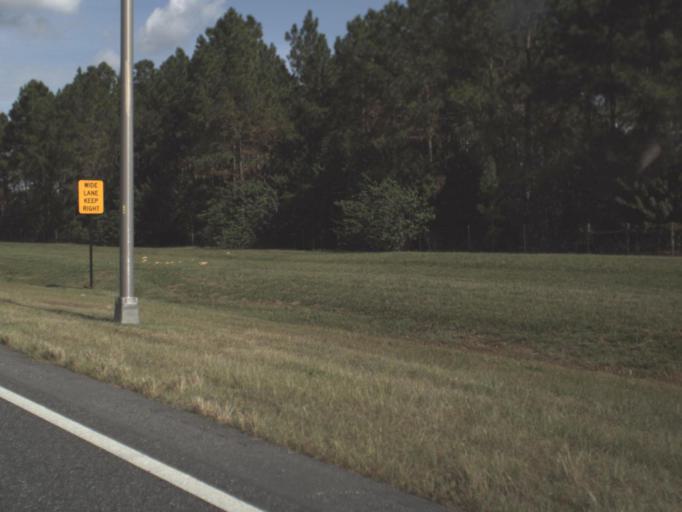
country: US
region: Florida
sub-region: Polk County
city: Auburndale
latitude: 28.1082
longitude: -81.8314
